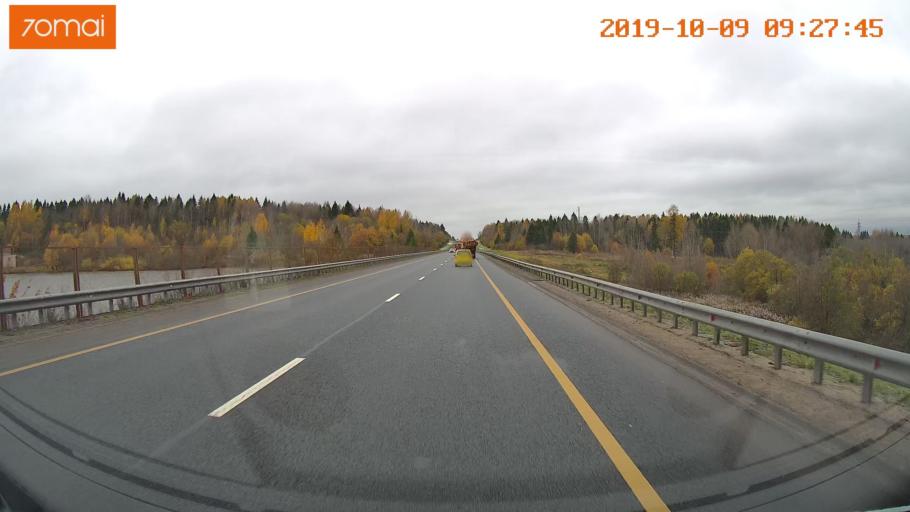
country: RU
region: Vologda
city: Vologda
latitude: 59.1163
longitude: 39.9749
